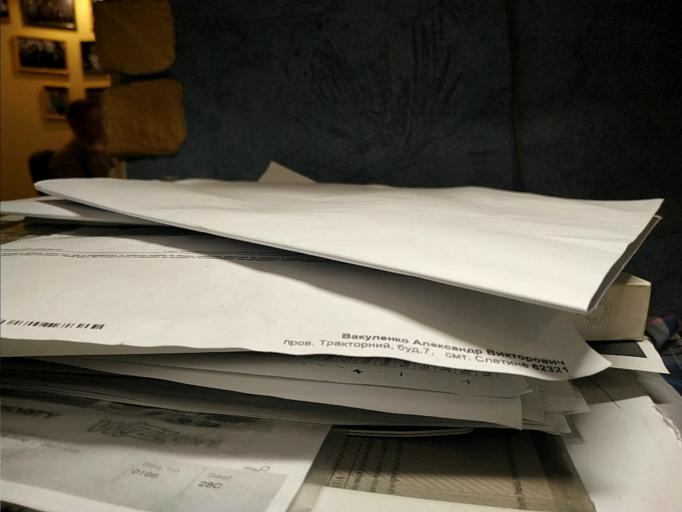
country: RU
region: Tverskaya
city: Zubtsov
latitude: 56.1137
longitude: 34.6107
